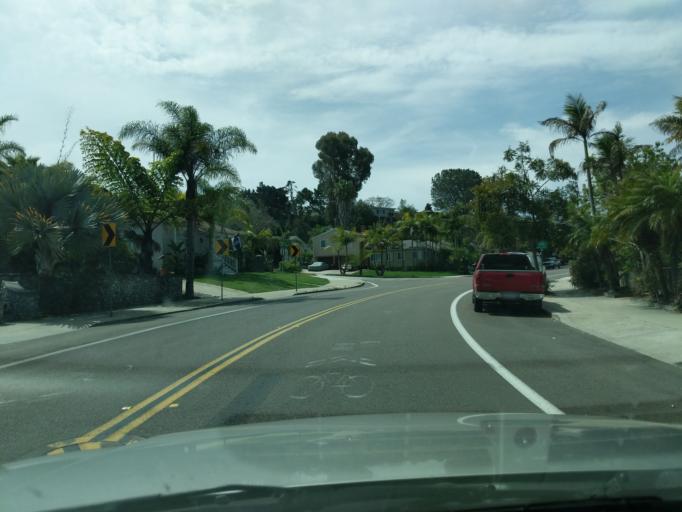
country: US
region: California
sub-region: San Diego County
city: Coronado
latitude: 32.7387
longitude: -117.2369
